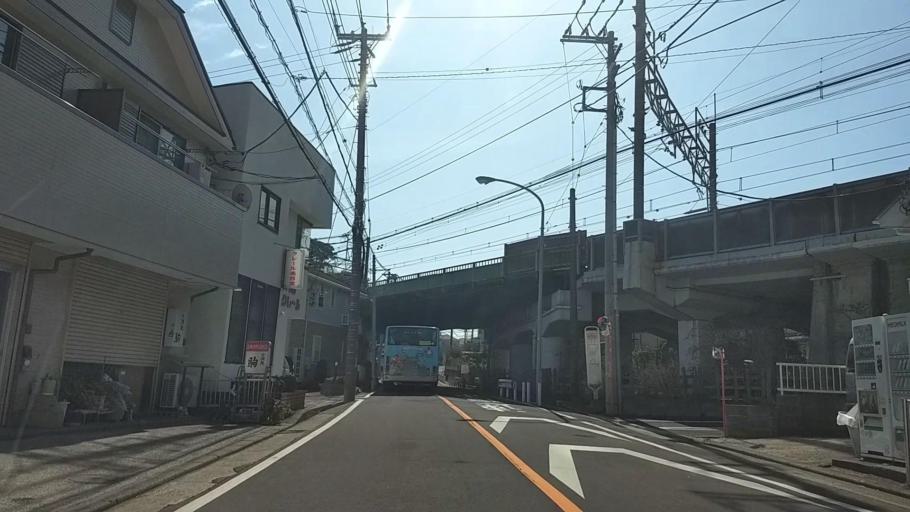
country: JP
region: Kanagawa
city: Kamakura
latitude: 35.3688
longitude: 139.5391
